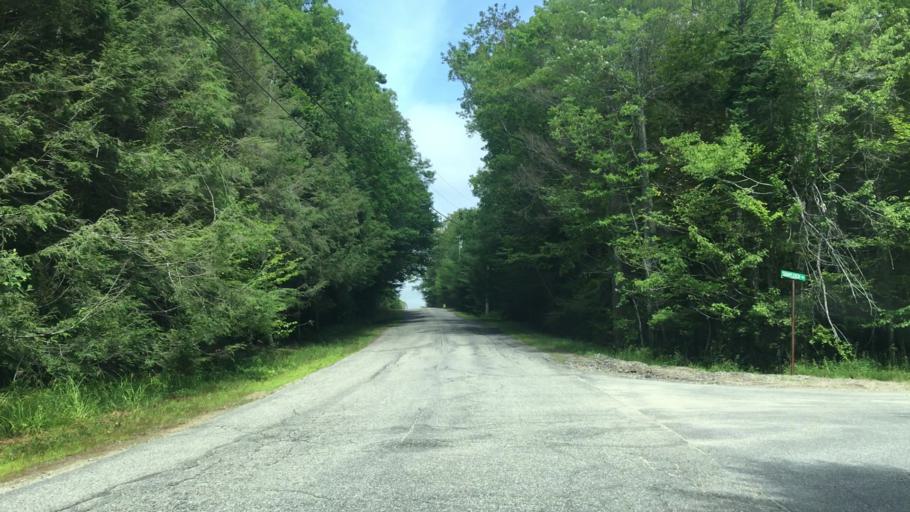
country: US
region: Maine
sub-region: Cumberland County
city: Brunswick
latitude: 43.8501
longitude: -69.9061
